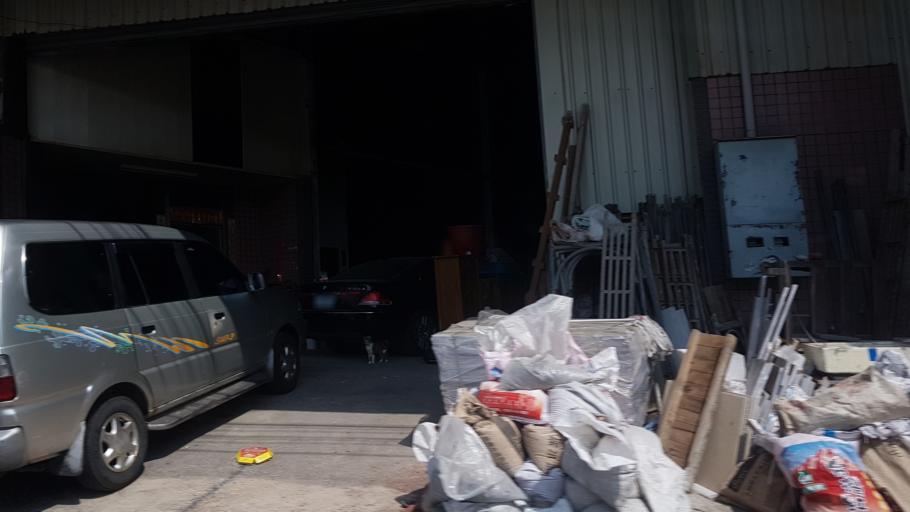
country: TW
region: Taiwan
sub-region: Tainan
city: Tainan
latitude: 22.9357
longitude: 120.2493
